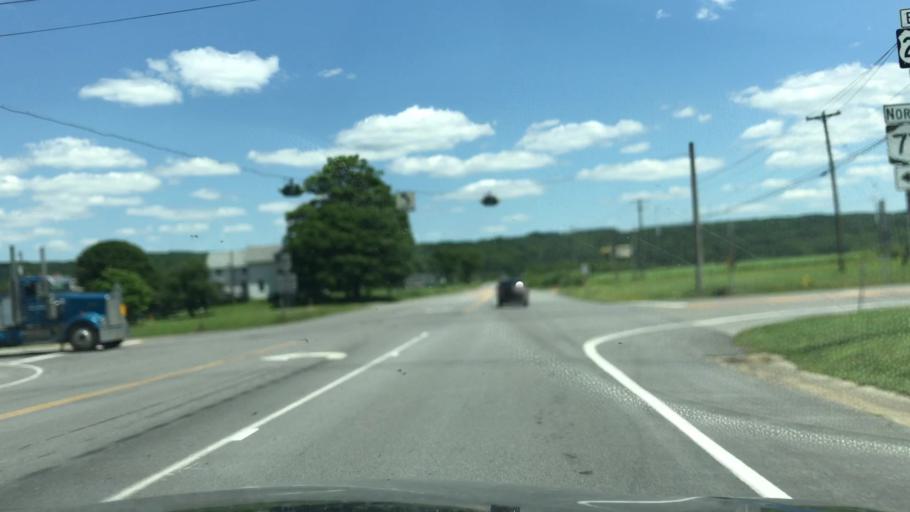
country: US
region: New York
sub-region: Wyoming County
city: Attica
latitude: 42.7703
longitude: -78.3892
